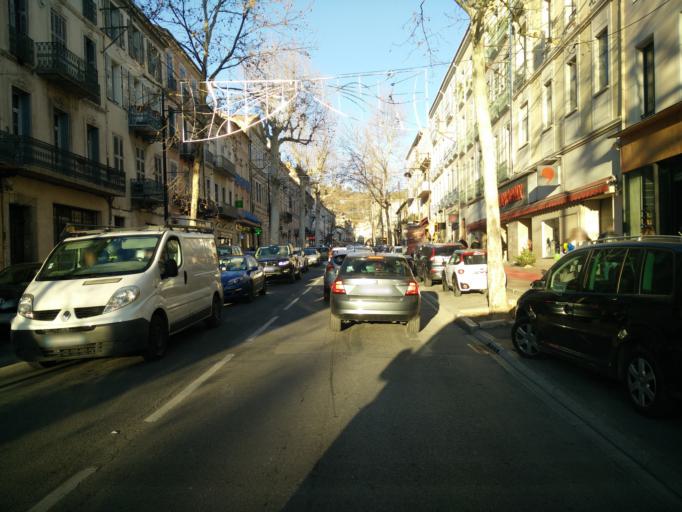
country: FR
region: Provence-Alpes-Cote d'Azur
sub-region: Departement du Var
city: Draguignan
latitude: 43.5382
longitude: 6.4621
